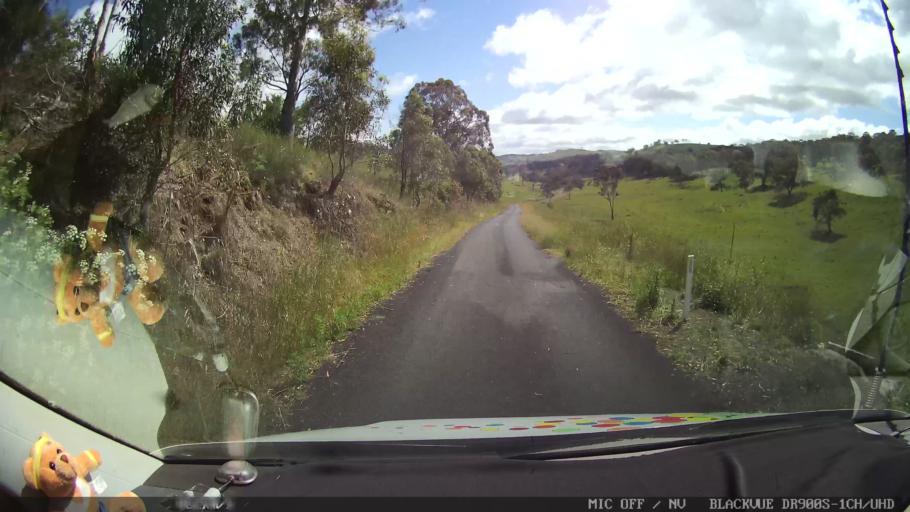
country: AU
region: New South Wales
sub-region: Guyra
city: Guyra
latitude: -30.0007
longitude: 151.6723
